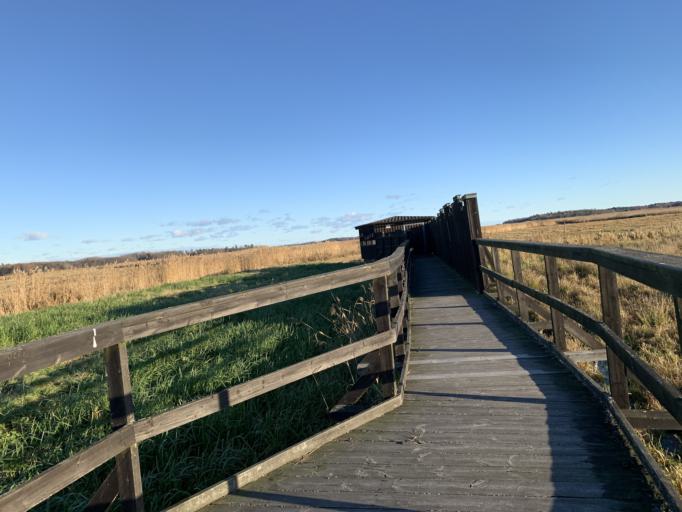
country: SE
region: Soedermanland
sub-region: Eskilstuna Kommun
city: Torshalla
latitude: 59.5215
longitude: 16.4528
